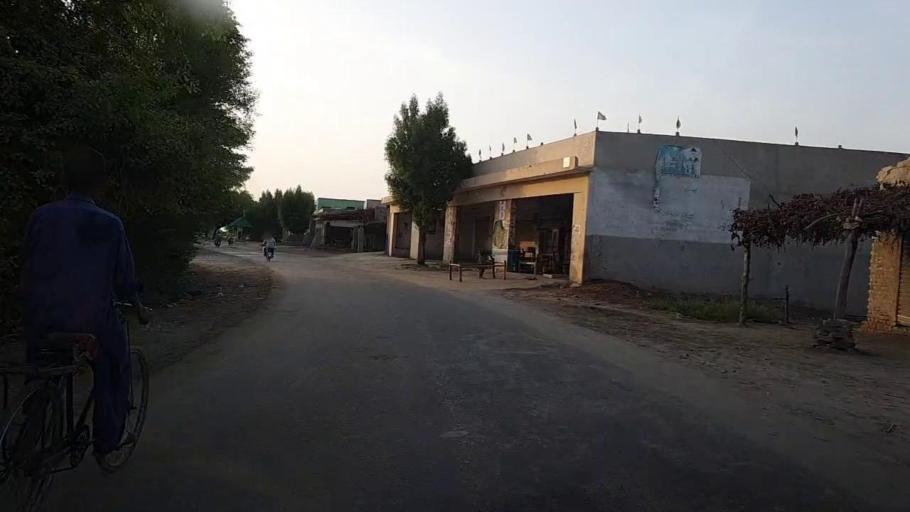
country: PK
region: Sindh
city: Ubauro
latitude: 28.2199
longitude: 69.8207
